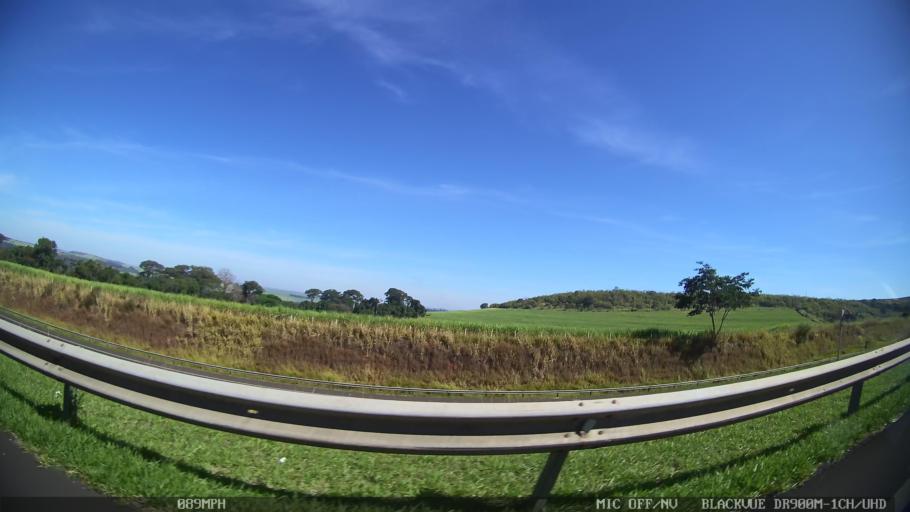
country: BR
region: Sao Paulo
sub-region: Santa Rita Do Passa Quatro
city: Santa Rita do Passa Quatro
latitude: -21.7139
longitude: -47.5910
